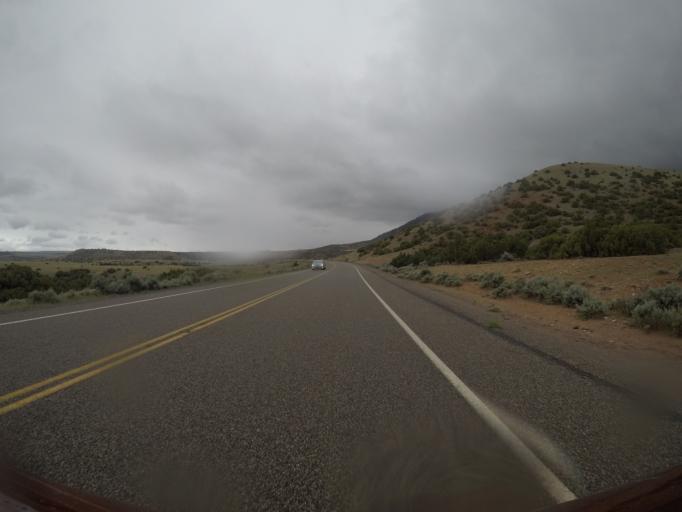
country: US
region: Wyoming
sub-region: Big Horn County
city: Lovell
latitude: 45.0691
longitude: -108.2550
